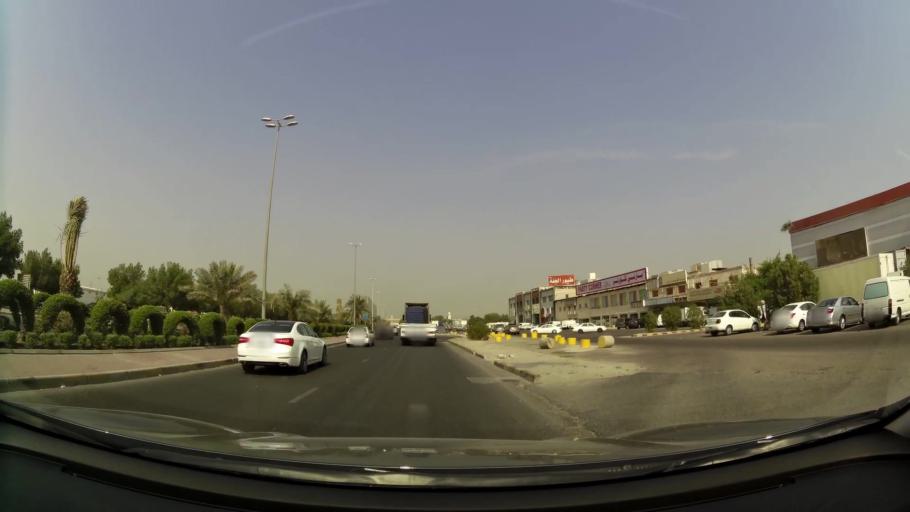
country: KW
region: Al Asimah
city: Ar Rabiyah
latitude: 29.3202
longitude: 47.9245
